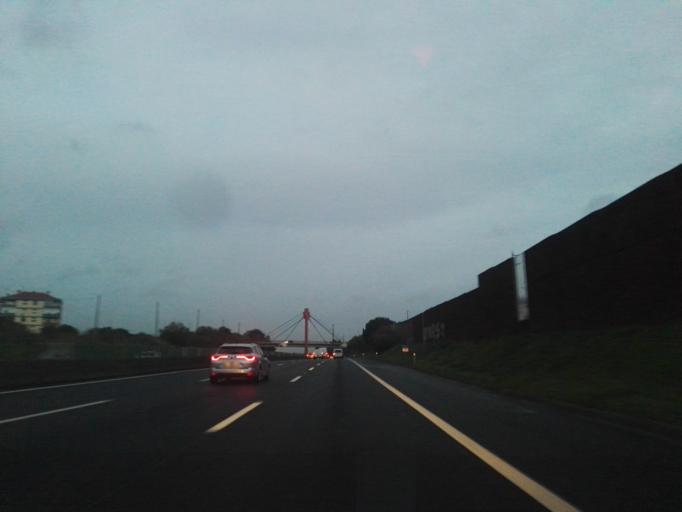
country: PT
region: Setubal
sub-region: Seixal
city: Amora
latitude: 38.6190
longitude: -9.1277
